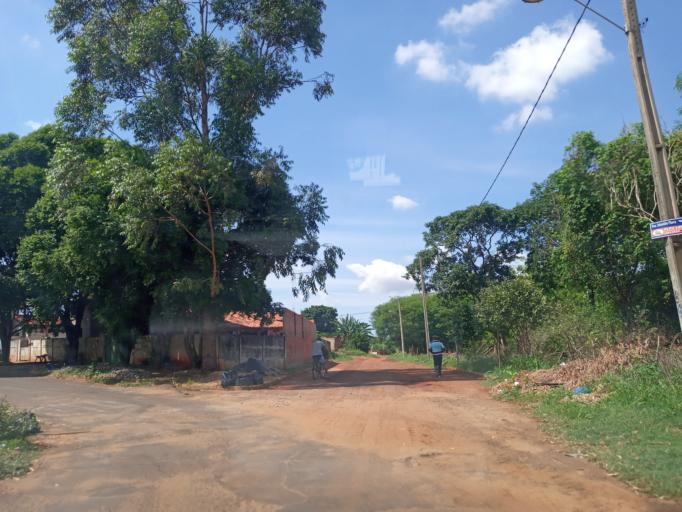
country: BR
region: Minas Gerais
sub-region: Ituiutaba
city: Ituiutaba
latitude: -18.9943
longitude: -49.4761
